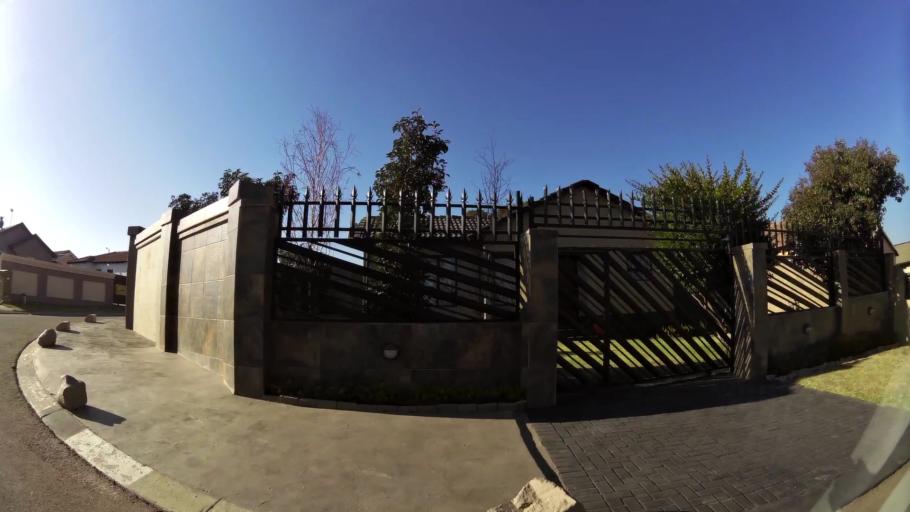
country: ZA
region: Gauteng
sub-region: City of Johannesburg Metropolitan Municipality
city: Modderfontein
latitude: -26.0442
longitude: 28.1615
